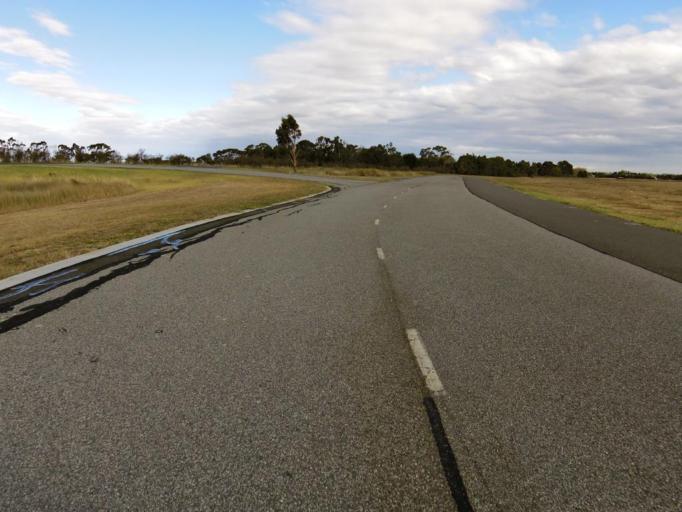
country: AU
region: Victoria
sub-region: Casey
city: Cranbourne East
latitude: -38.1257
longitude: 145.3154
